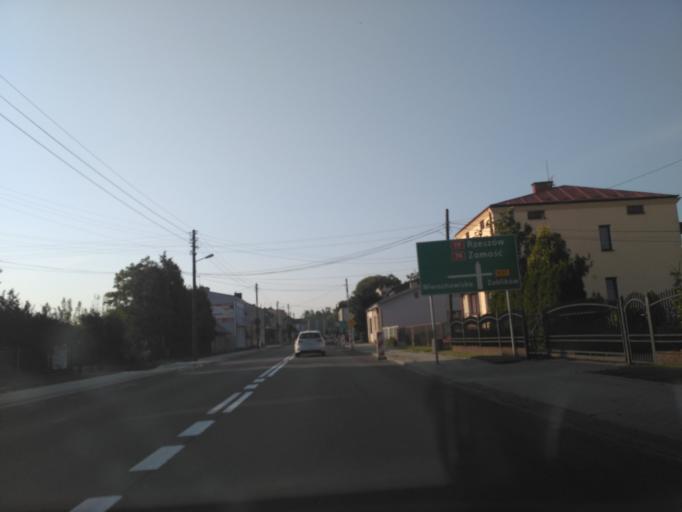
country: PL
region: Lublin Voivodeship
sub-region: Powiat janowski
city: Modliborzyce
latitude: 50.7554
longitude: 22.3286
